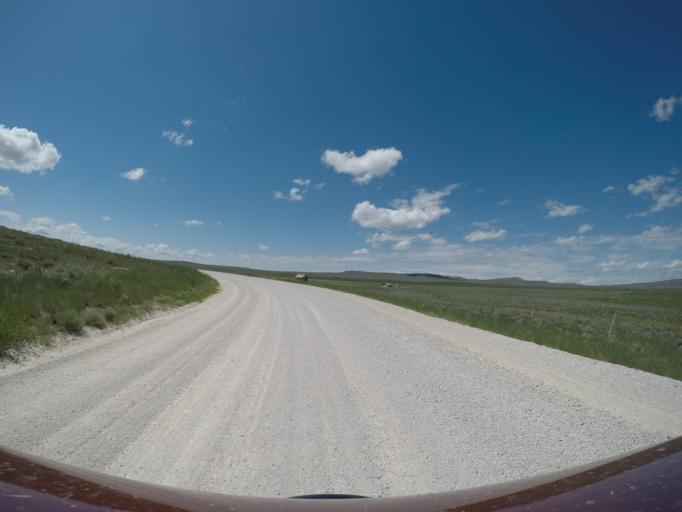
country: US
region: Wyoming
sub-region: Park County
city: Powell
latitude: 45.2066
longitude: -108.7277
